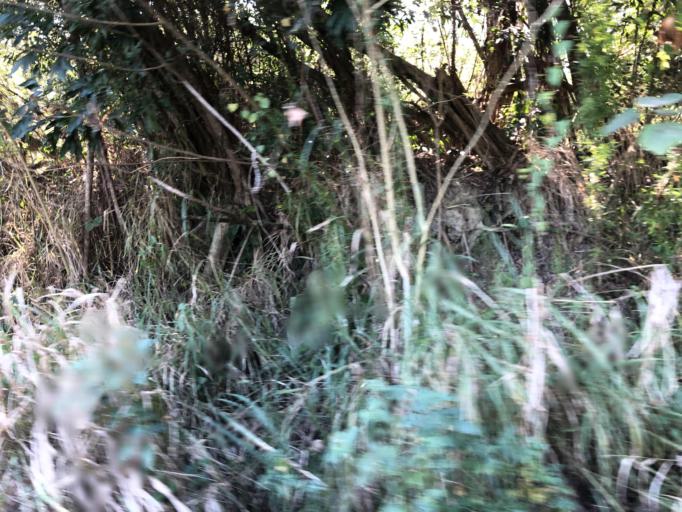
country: TW
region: Taiwan
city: Yujing
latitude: 23.0490
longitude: 120.3723
